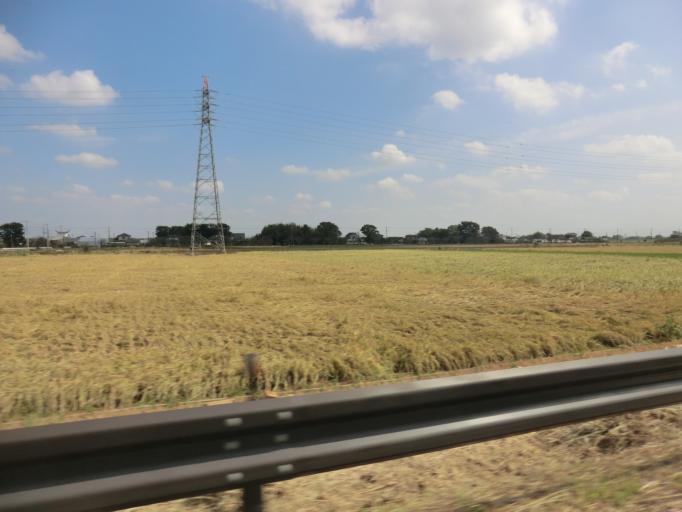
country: JP
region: Ibaraki
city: Mitsukaido
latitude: 36.0674
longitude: 139.9900
